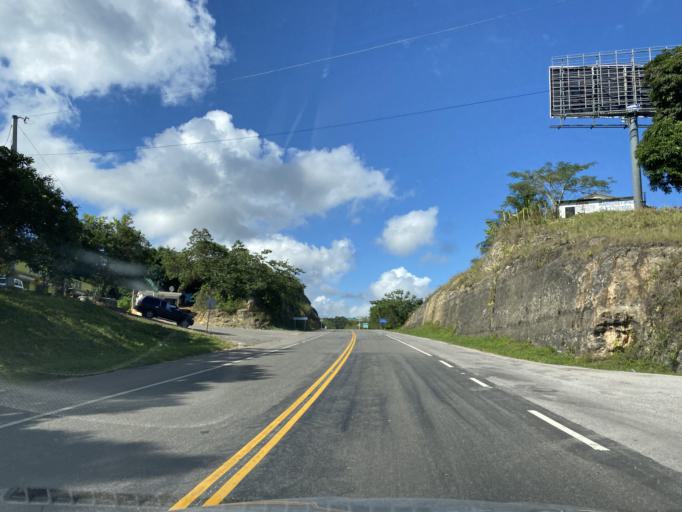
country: DO
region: Monte Plata
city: Majagual
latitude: 19.0420
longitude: -69.8295
